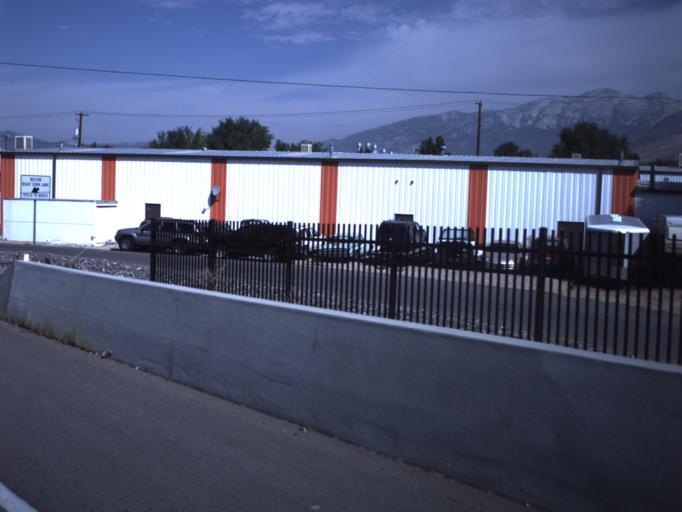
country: US
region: Utah
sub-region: Utah County
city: Pleasant Grove
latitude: 40.3605
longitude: -111.7460
